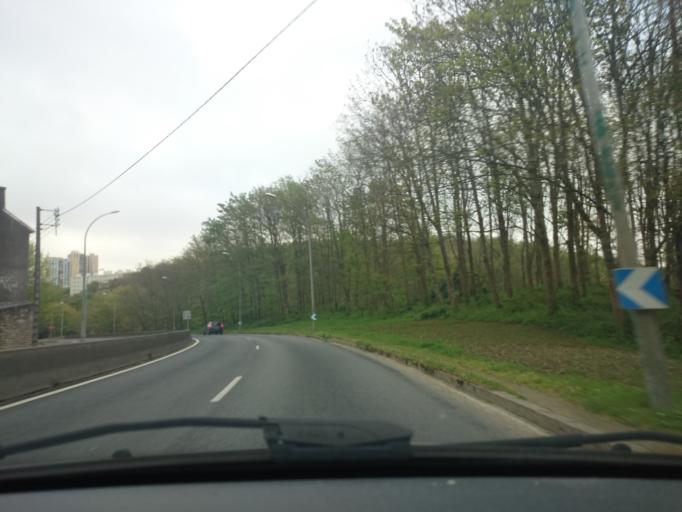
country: FR
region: Brittany
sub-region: Departement du Finistere
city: Bohars
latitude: 48.4103
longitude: -4.5254
